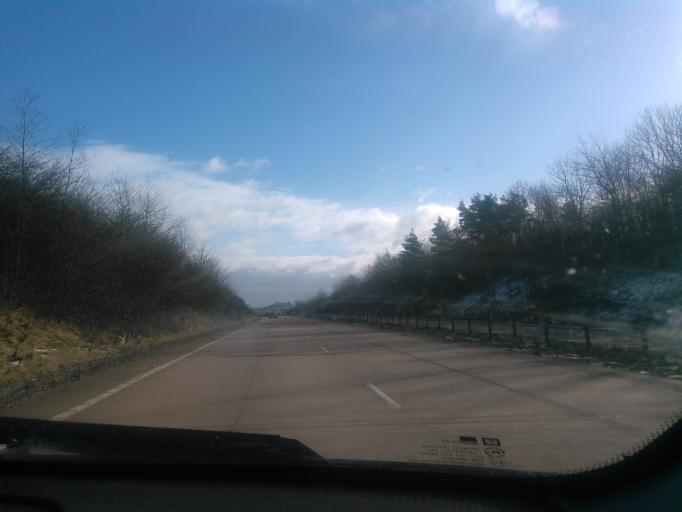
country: GB
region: England
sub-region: Staffordshire
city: Cheadle
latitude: 52.9279
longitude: -1.9465
